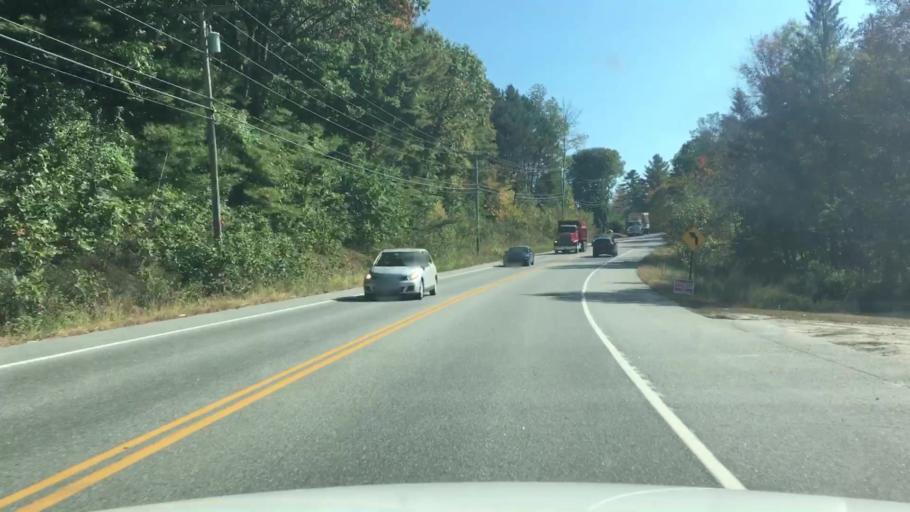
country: US
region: Maine
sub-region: Androscoggin County
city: Lisbon Falls
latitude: 43.9911
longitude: -70.0471
